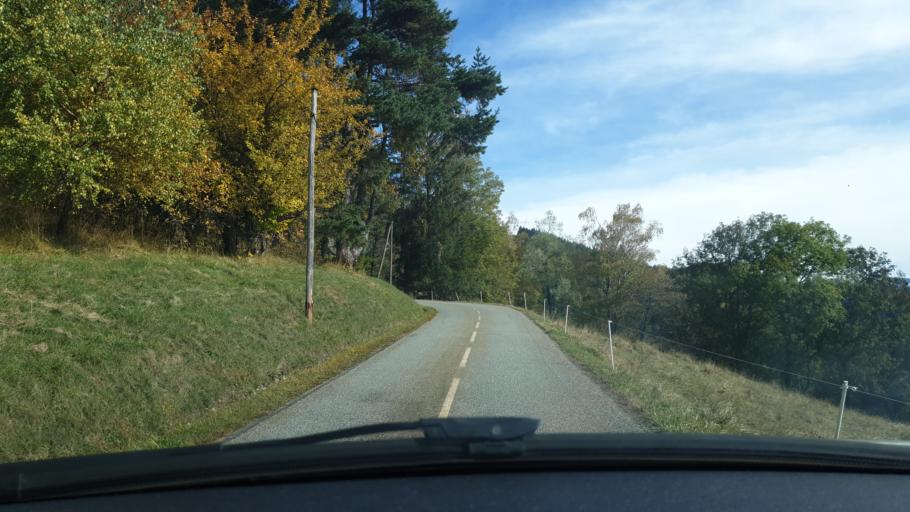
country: FR
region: Rhone-Alpes
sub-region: Departement de la Savoie
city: Aiton
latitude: 45.5031
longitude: 6.2182
